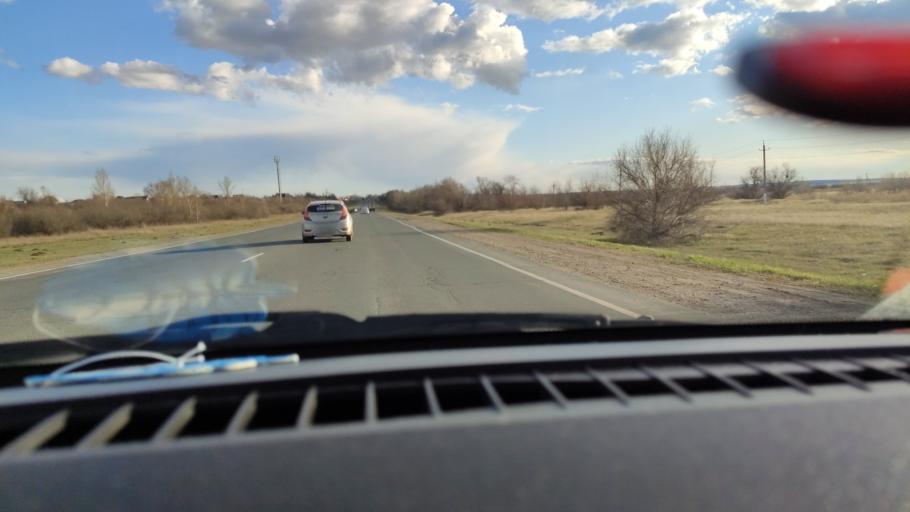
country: RU
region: Saratov
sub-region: Saratovskiy Rayon
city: Saratov
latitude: 51.6852
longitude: 46.0033
